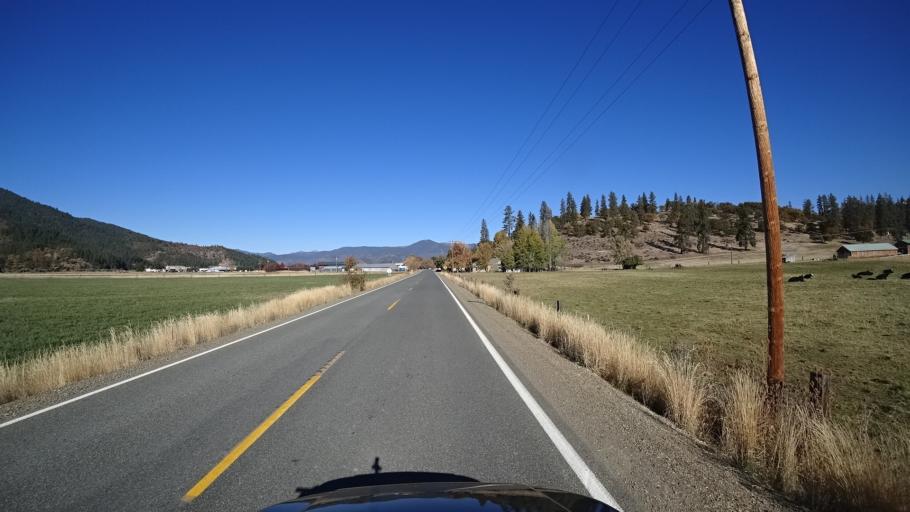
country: US
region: California
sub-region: Siskiyou County
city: Yreka
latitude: 41.5980
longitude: -122.8441
